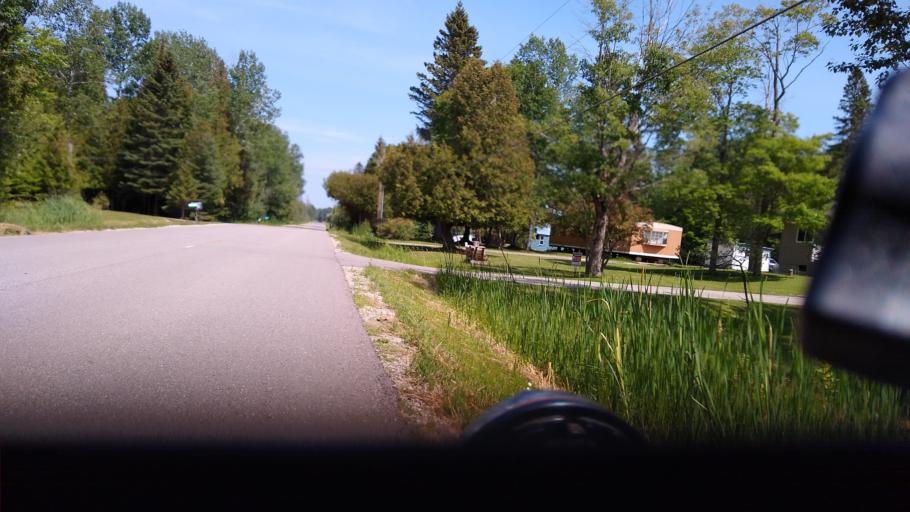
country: US
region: Michigan
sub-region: Delta County
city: Escanaba
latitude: 45.7100
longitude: -87.1160
